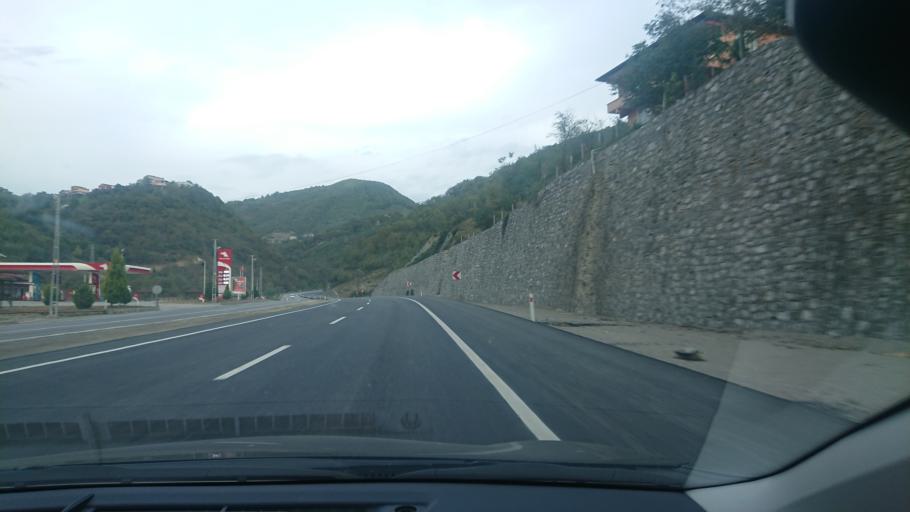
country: TR
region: Zonguldak
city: Beycuma
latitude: 41.3849
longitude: 31.9416
